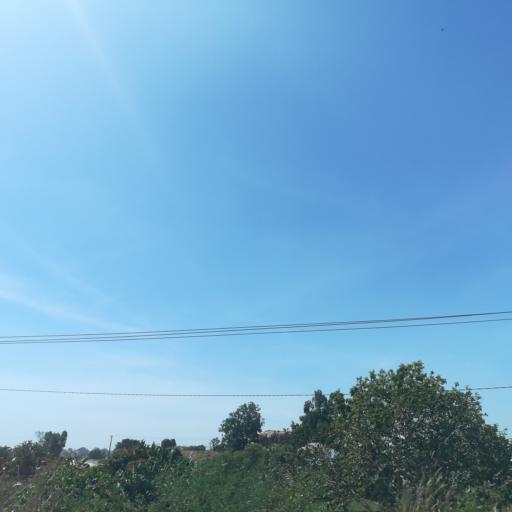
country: NG
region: Plateau
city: Bukuru
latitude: 9.7856
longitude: 8.8801
